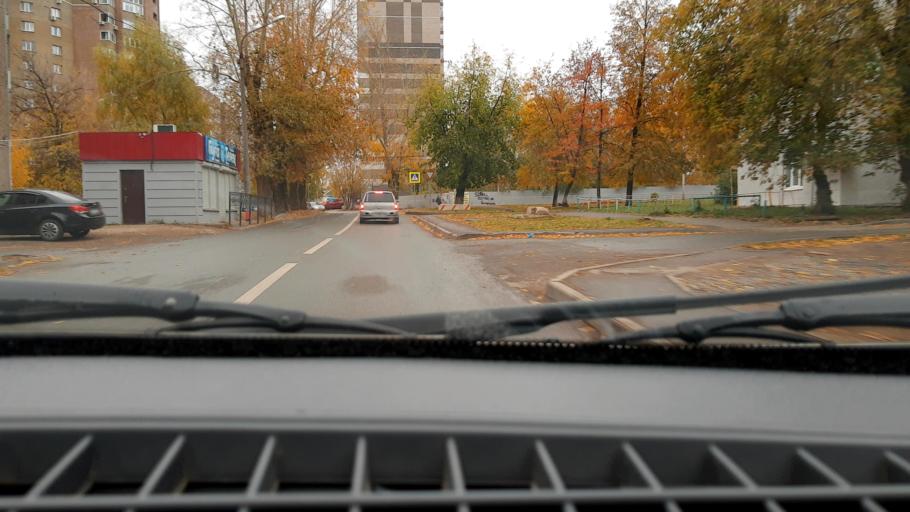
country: RU
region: Bashkortostan
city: Ufa
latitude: 54.8062
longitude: 56.1284
